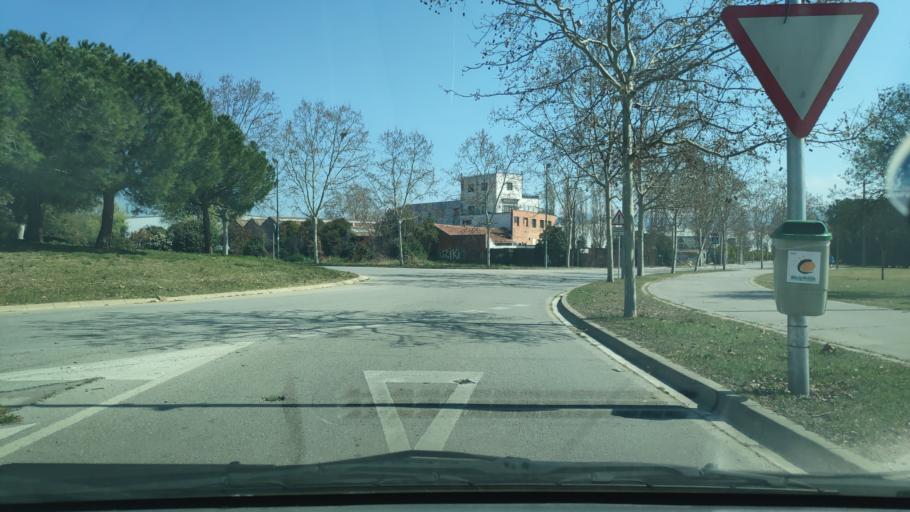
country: ES
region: Catalonia
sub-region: Provincia de Barcelona
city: Santa Perpetua de Mogoda
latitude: 41.5362
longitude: 2.1855
